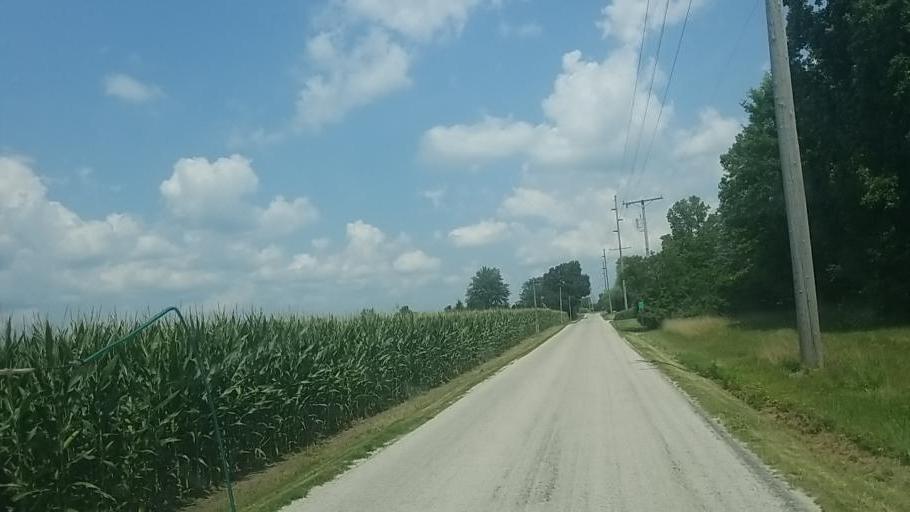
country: US
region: Ohio
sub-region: Crawford County
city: Bucyrus
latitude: 40.7912
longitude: -82.9980
